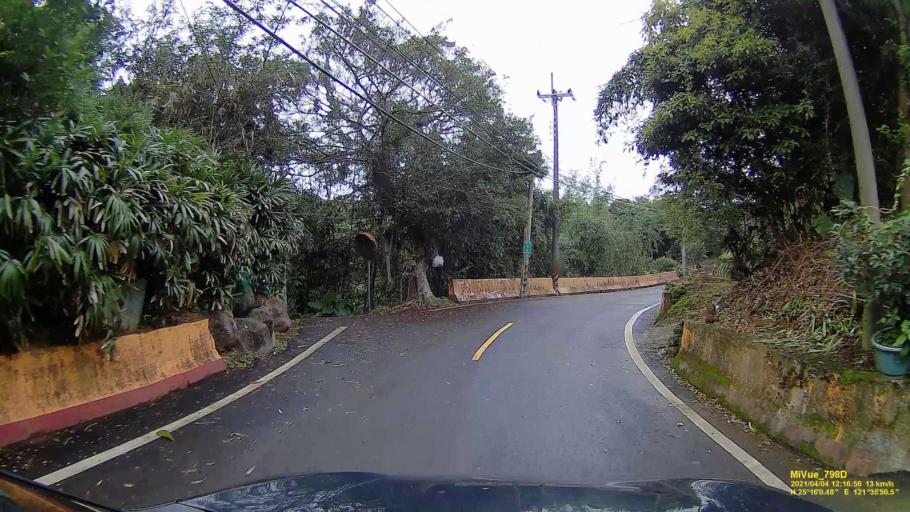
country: TW
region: Taiwan
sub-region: Keelung
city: Keelung
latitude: 25.2668
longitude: 121.5975
